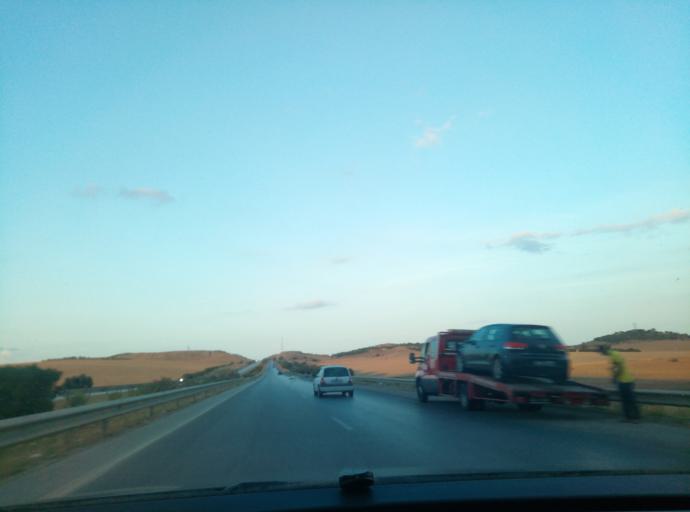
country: TN
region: Manouba
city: Manouba
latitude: 36.7550
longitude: 10.0474
